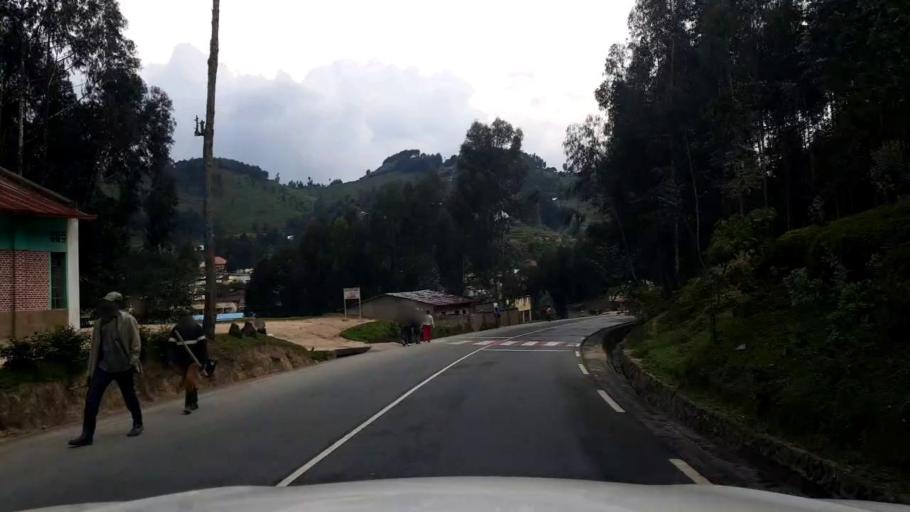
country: RW
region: Northern Province
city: Musanze
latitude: -1.6841
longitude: 29.5168
